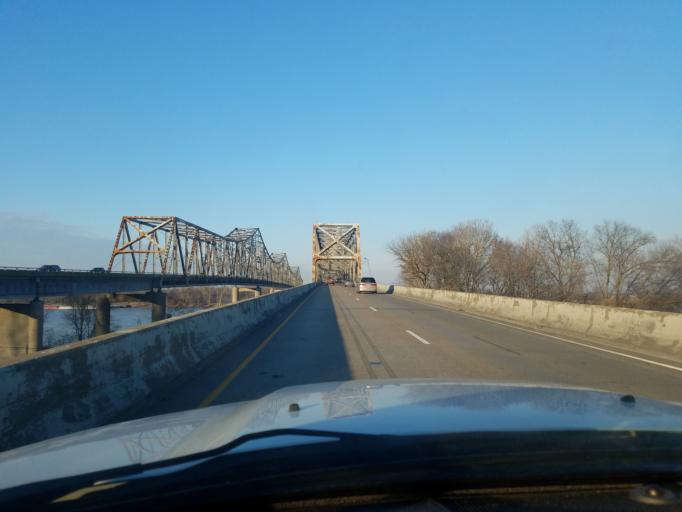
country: US
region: Indiana
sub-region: Vanderburgh County
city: Evansville
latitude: 37.9016
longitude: -87.5519
